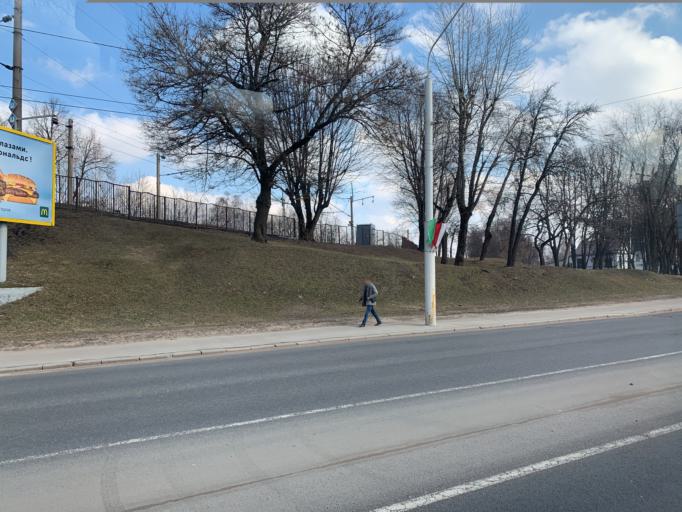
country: BY
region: Minsk
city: Minsk
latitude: 53.8880
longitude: 27.5640
